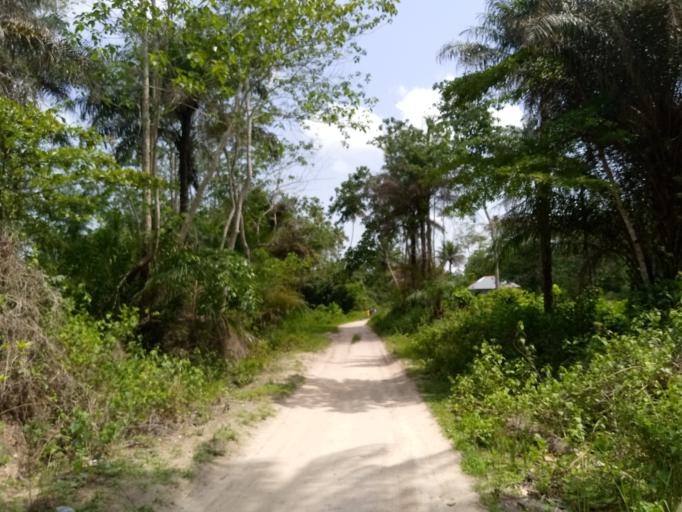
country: SL
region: Western Area
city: Waterloo
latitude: 8.3653
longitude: -13.0018
